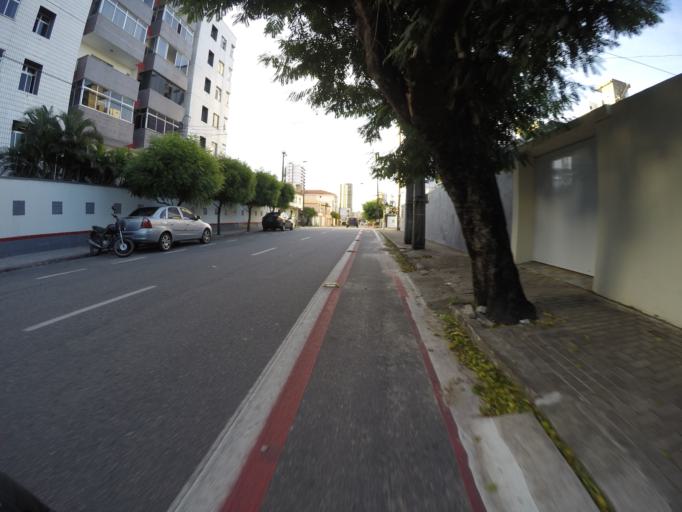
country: BR
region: Ceara
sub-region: Fortaleza
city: Fortaleza
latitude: -3.7439
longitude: -38.5143
